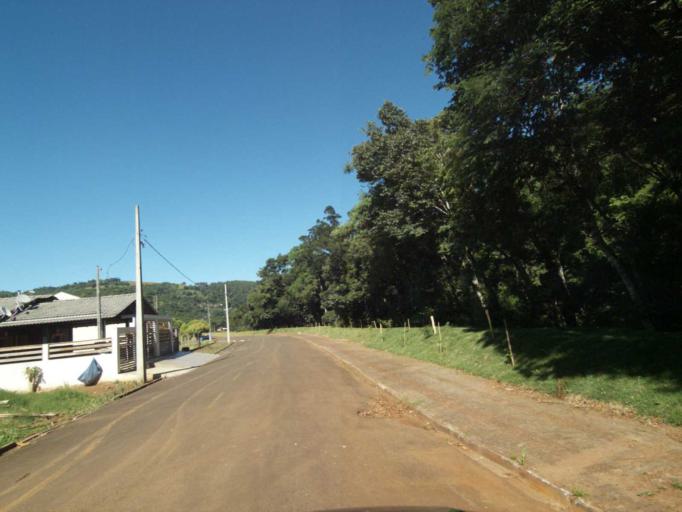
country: BR
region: Parana
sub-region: Francisco Beltrao
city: Francisco Beltrao
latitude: -26.1422
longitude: -53.3097
